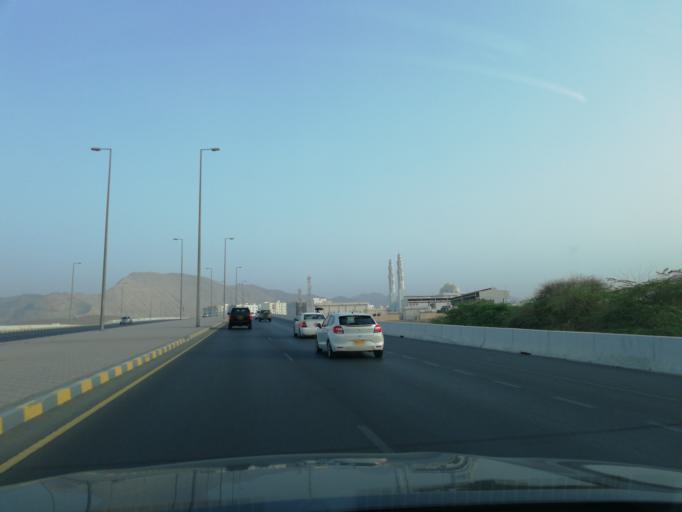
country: OM
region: Muhafazat Masqat
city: Bawshar
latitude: 23.5848
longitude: 58.4160
